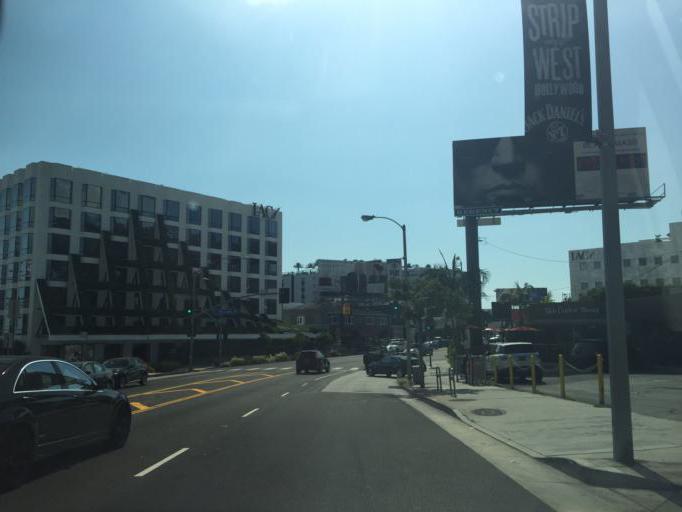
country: US
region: California
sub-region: Los Angeles County
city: West Hollywood
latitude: 34.0911
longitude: -118.3828
